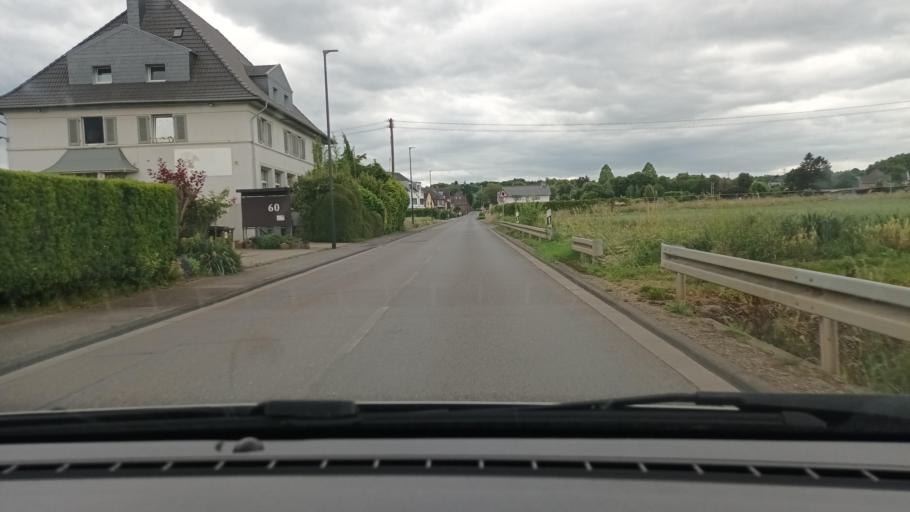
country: DE
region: North Rhine-Westphalia
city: Bruhl
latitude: 50.8640
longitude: 6.9050
